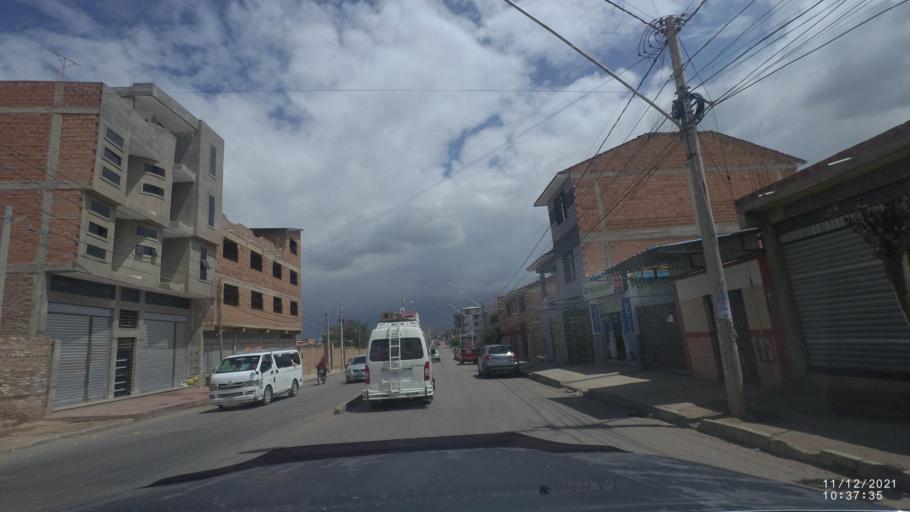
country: BO
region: Cochabamba
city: Cochabamba
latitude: -17.4447
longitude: -66.1251
